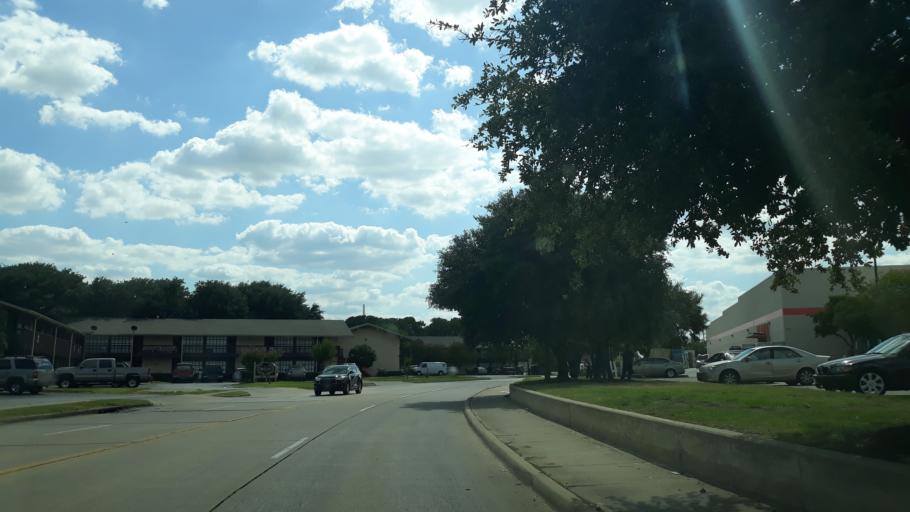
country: US
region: Texas
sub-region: Dallas County
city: Irving
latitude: 32.8332
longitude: -96.9896
